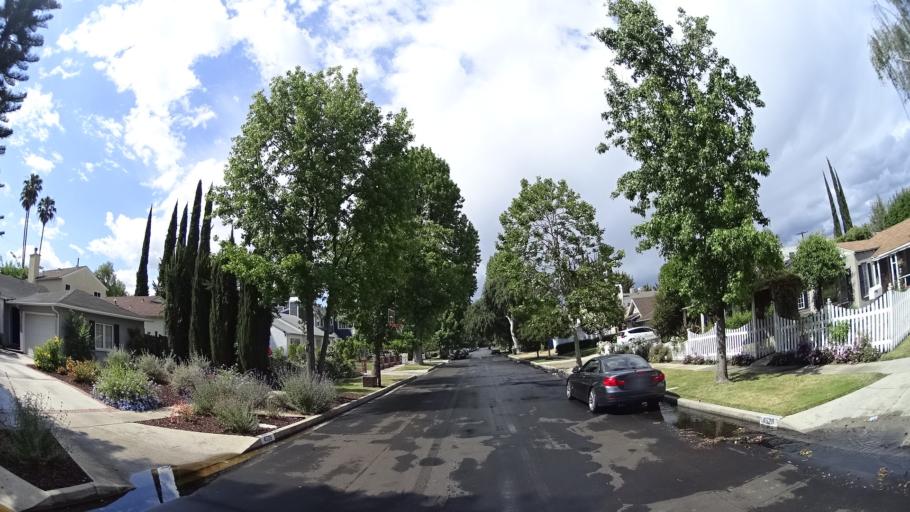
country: US
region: California
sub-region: Los Angeles County
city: Sherman Oaks
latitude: 34.1531
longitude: -118.4150
